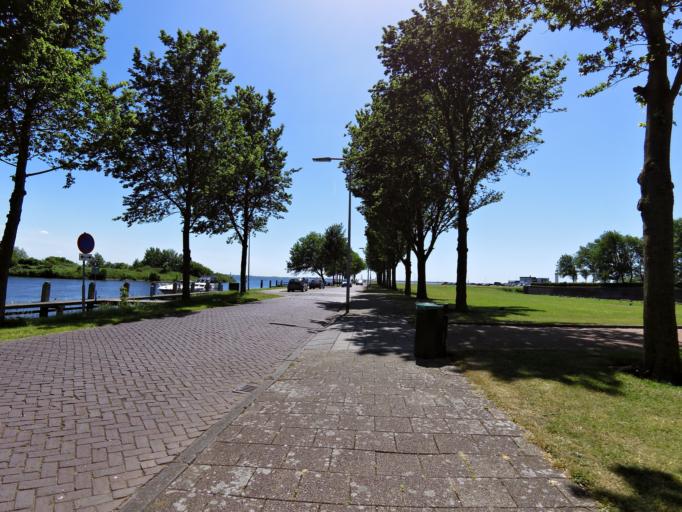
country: NL
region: South Holland
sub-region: Gemeente Hellevoetsluis
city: Hellevoetsluis
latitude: 51.8217
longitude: 4.1321
